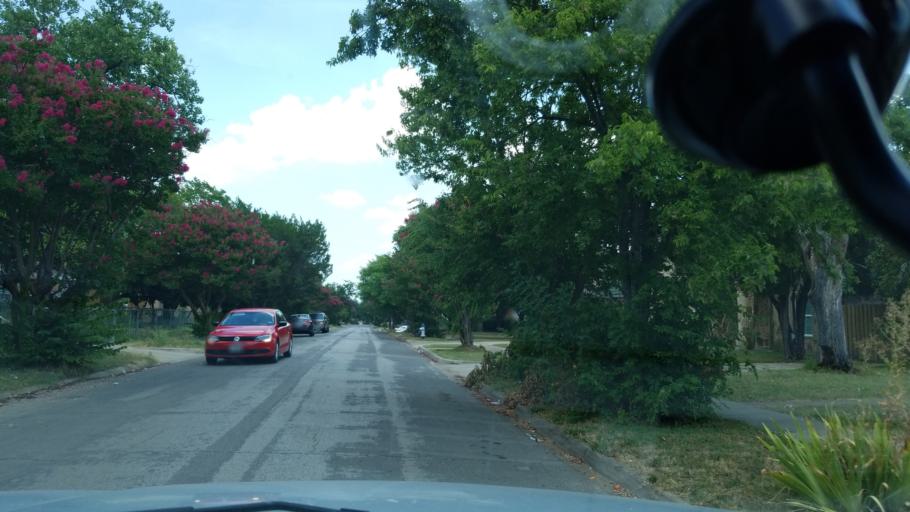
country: US
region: Texas
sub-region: Dallas County
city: Cockrell Hill
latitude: 32.7263
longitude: -96.8710
